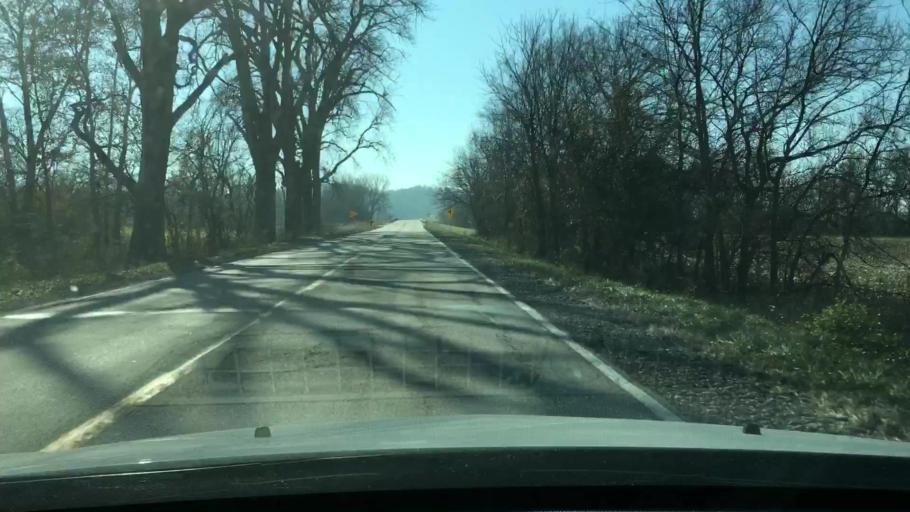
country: US
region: Illinois
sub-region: Morgan County
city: Meredosia
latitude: 39.7140
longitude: -90.5686
